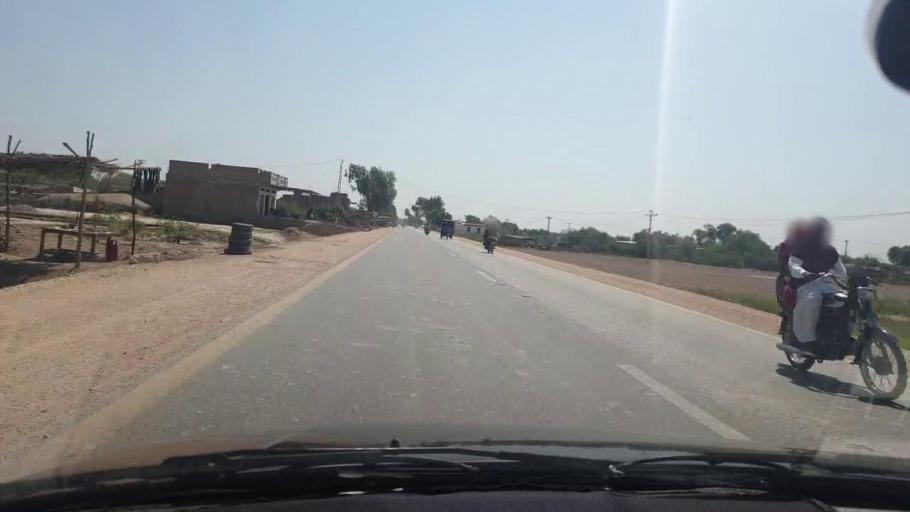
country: PK
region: Sindh
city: Tando Allahyar
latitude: 25.4349
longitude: 68.7432
